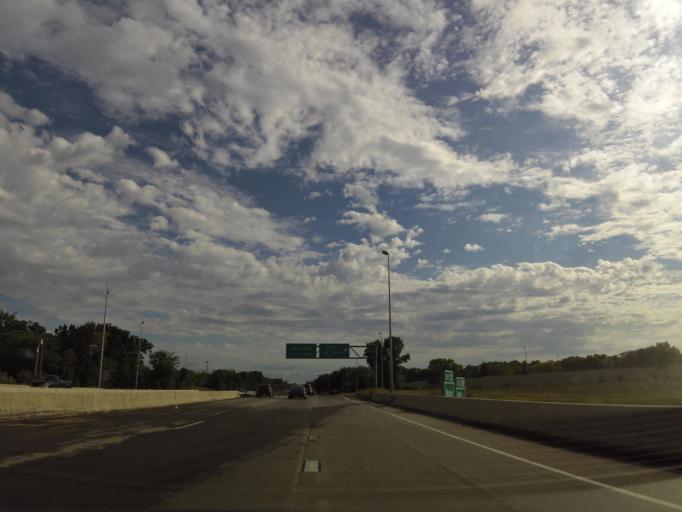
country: US
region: Minnesota
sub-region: Hennepin County
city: Osseo
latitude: 45.0835
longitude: -93.4023
